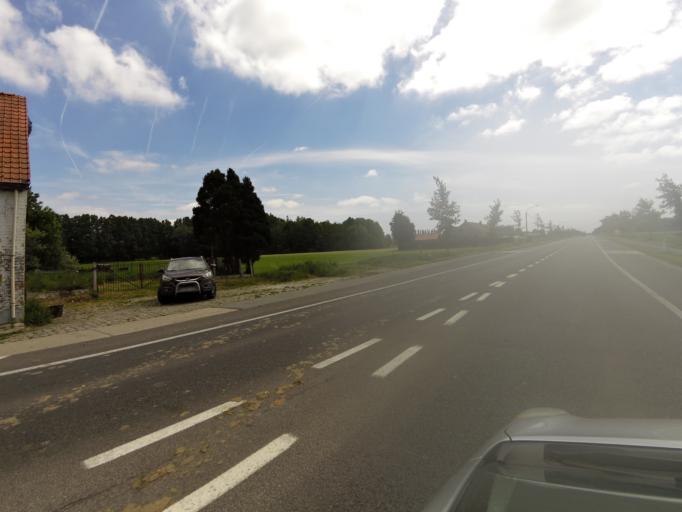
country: BE
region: Flanders
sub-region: Provincie West-Vlaanderen
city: Diksmuide
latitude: 51.0724
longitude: 2.8750
